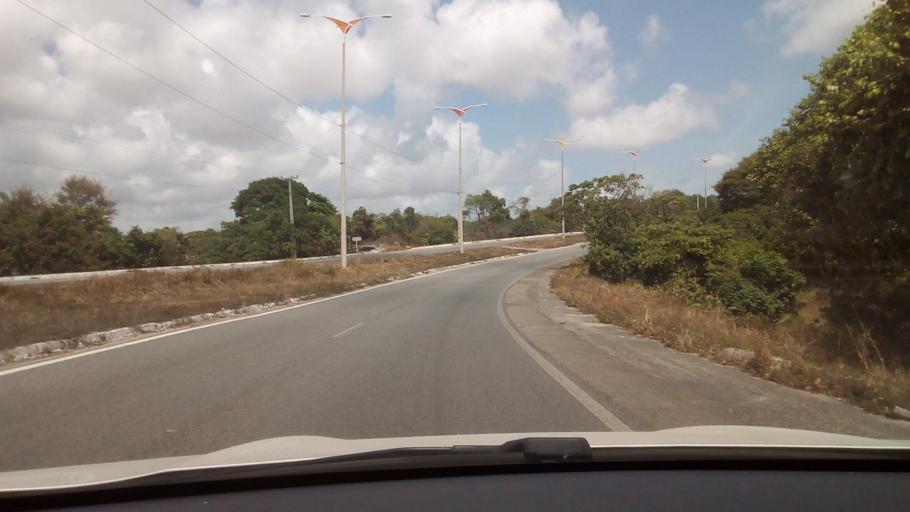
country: BR
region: Paraiba
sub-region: Joao Pessoa
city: Joao Pessoa
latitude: -7.1819
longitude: -34.8059
